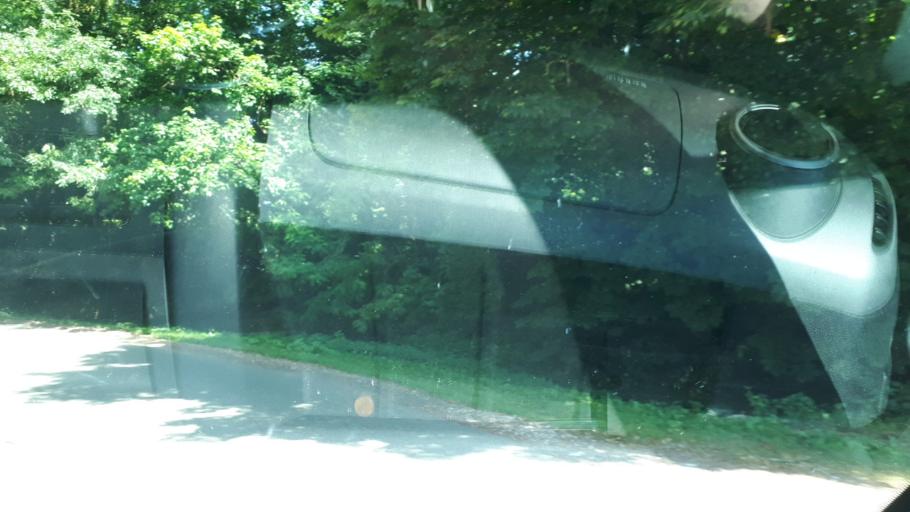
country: FR
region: Centre
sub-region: Departement d'Eure-et-Loir
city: Arrou
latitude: 48.0793
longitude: 1.1333
